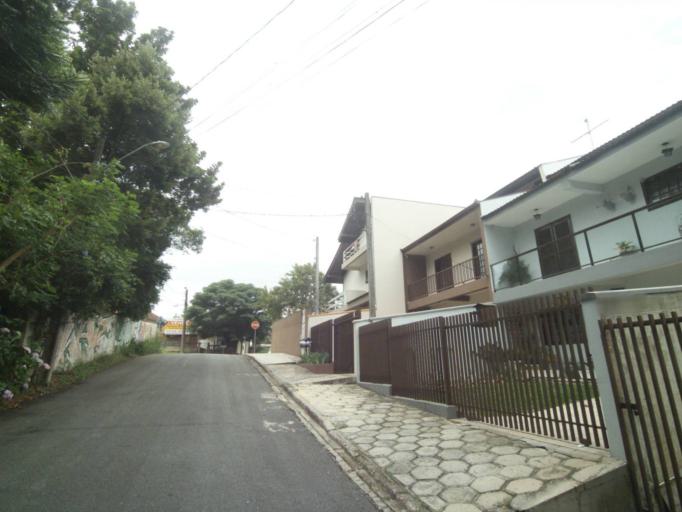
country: BR
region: Parana
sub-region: Curitiba
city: Curitiba
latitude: -25.4132
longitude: -49.2962
